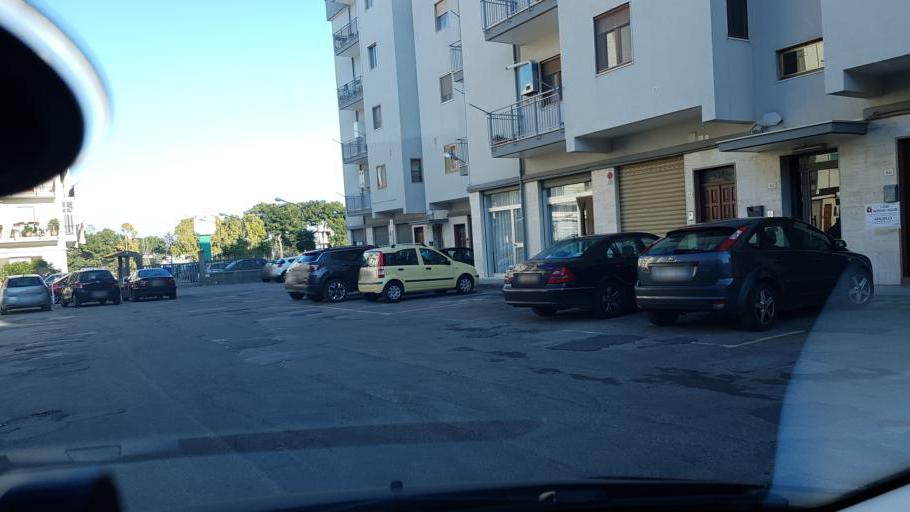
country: IT
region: Apulia
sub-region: Provincia di Brindisi
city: Ostuni
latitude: 40.7235
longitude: 17.5823
